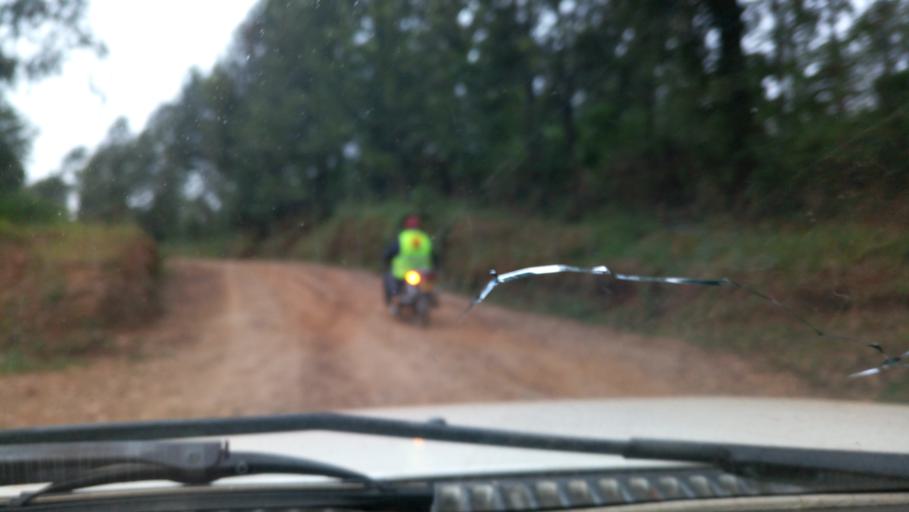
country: KE
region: Murang'a District
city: Kangema
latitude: -0.6778
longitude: 36.9778
